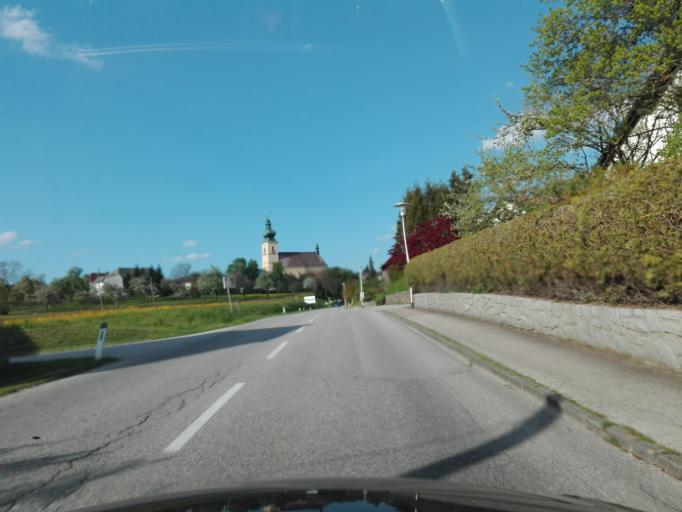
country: AT
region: Upper Austria
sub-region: Politischer Bezirk Rohrbach
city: Kleinzell im Muehlkreis
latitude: 48.4828
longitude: 13.9655
